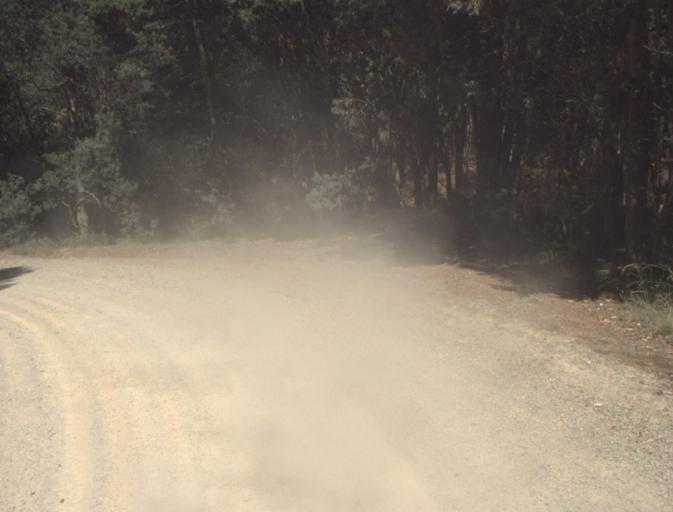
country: AU
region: Tasmania
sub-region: Dorset
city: Scottsdale
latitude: -41.3624
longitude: 147.4628
